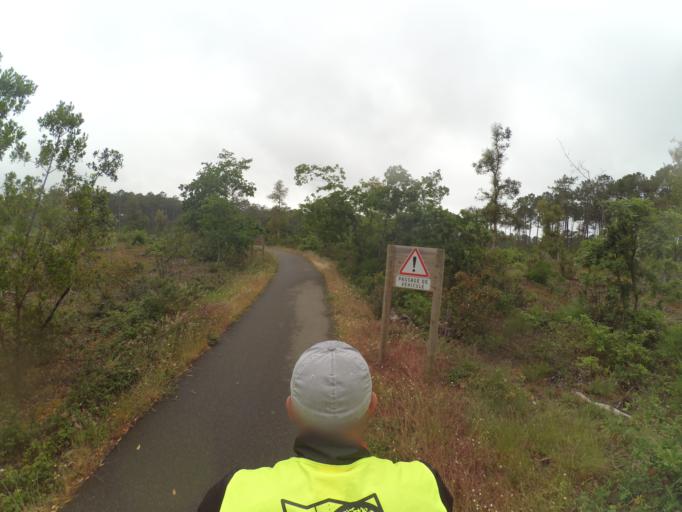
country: FR
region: Aquitaine
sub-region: Departement des Landes
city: Mimizan
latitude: 44.2200
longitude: -1.2421
